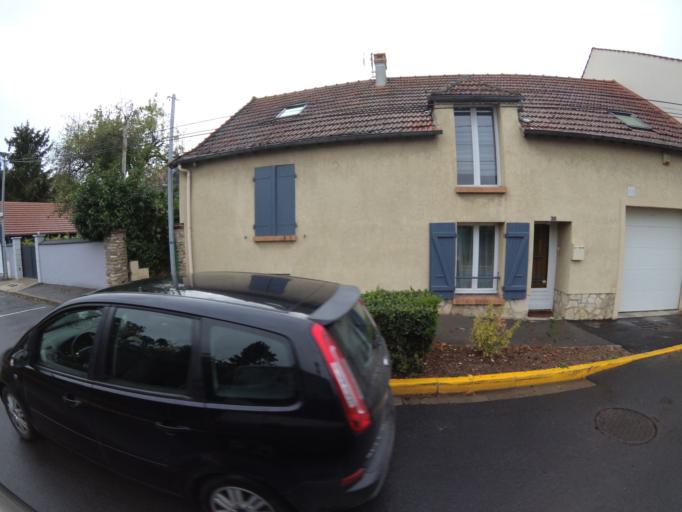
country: FR
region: Ile-de-France
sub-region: Departement de Seine-et-Marne
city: Chanteloup-en-Brie
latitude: 48.8551
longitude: 2.7387
